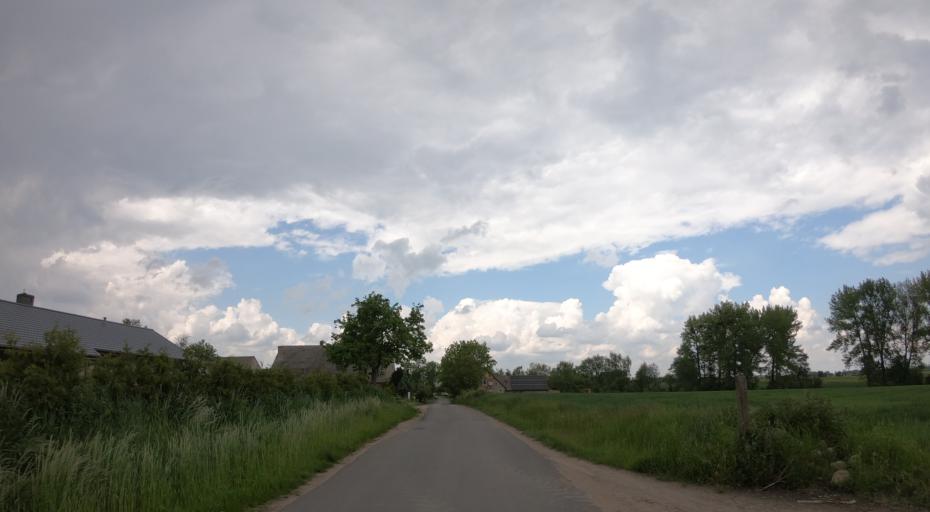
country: PL
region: West Pomeranian Voivodeship
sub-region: Powiat pyrzycki
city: Bielice
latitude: 53.2248
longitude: 14.7676
